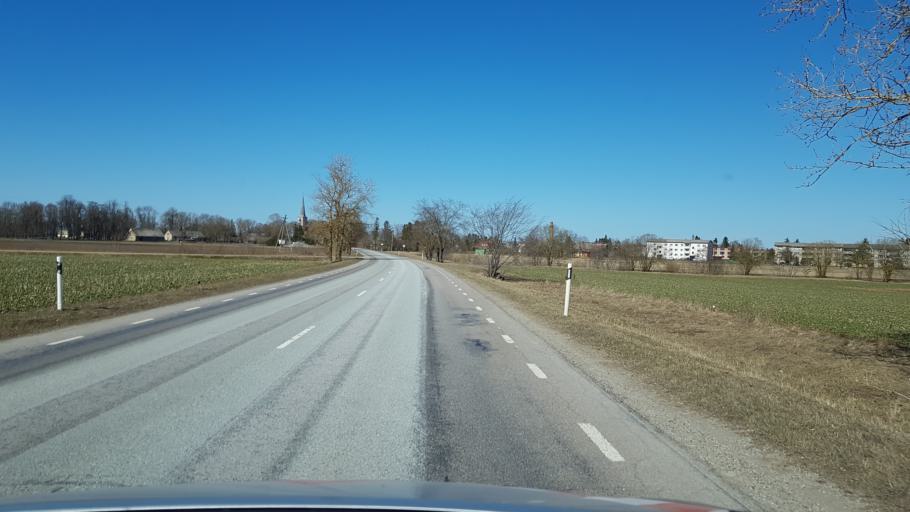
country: EE
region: Laeaene-Virumaa
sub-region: Viru-Nigula vald
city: Kunda
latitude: 59.4408
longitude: 26.6962
